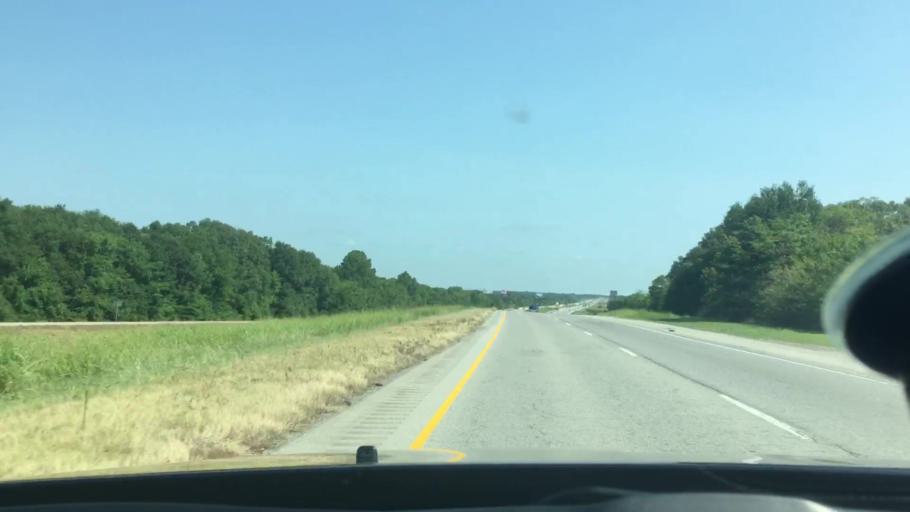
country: US
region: Oklahoma
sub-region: Atoka County
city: Atoka
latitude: 34.2367
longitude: -96.2207
